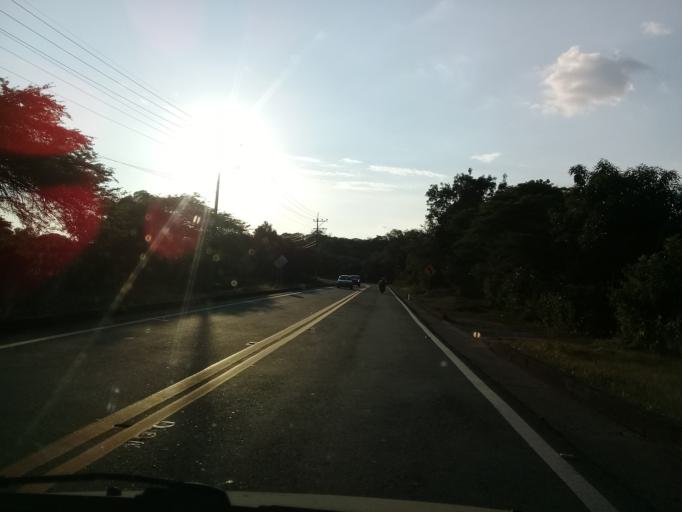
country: CO
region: Cundinamarca
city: Tocaima
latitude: 4.4344
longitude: -74.6855
